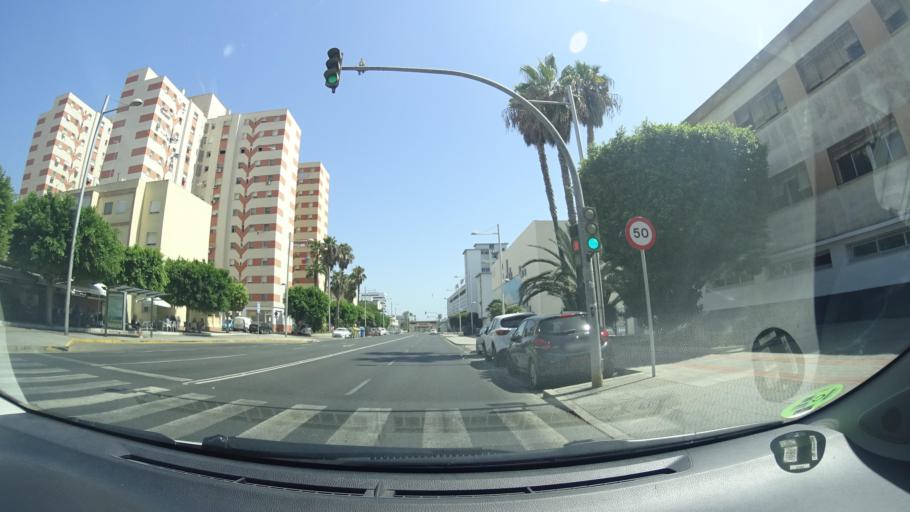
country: ES
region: Andalusia
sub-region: Provincia de Cadiz
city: Cadiz
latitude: 36.5052
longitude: -6.2731
